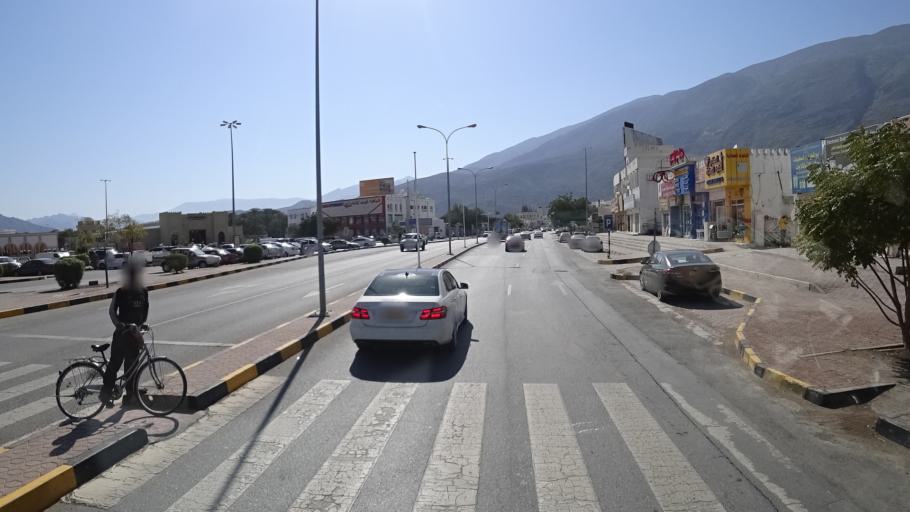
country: OM
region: Al Batinah
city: Rustaq
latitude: 23.3955
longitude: 57.4222
